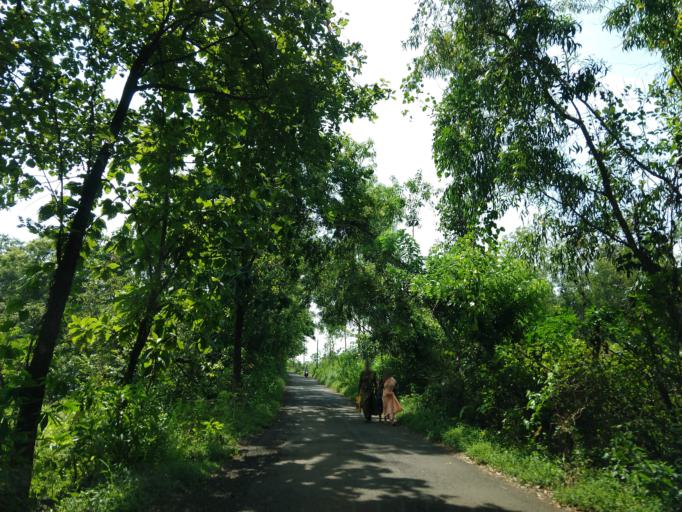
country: IN
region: Maharashtra
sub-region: Sindhudurg
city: Kudal
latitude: 16.0486
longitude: 73.6806
